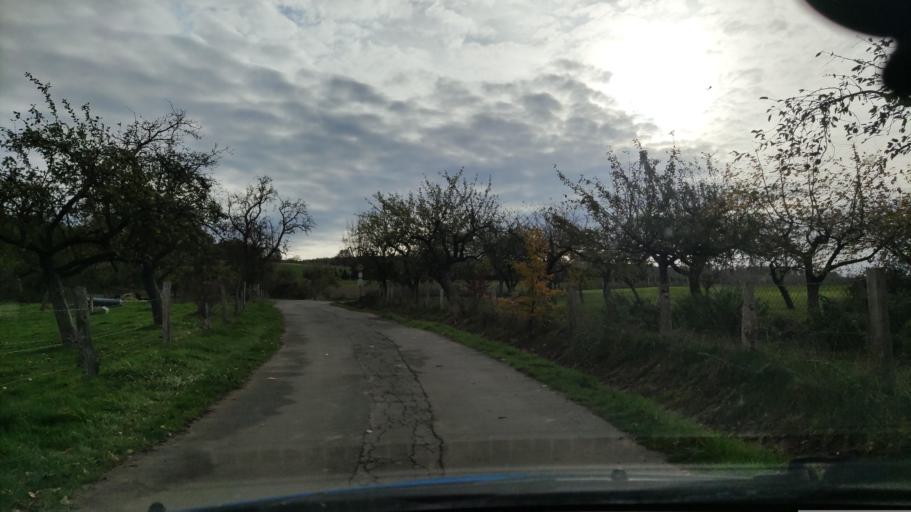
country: DE
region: Lower Saxony
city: Bodenfelde
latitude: 51.6194
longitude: 9.5622
